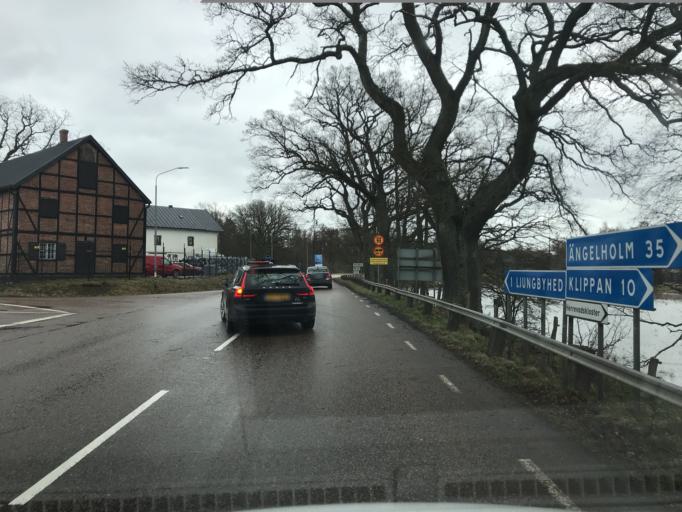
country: SE
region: Skane
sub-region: Klippans Kommun
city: Ljungbyhed
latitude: 56.0823
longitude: 13.2377
